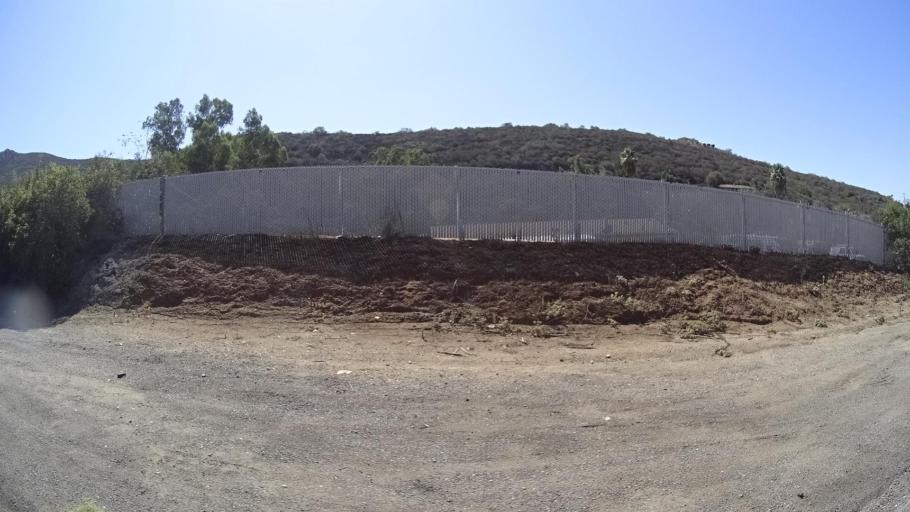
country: US
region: California
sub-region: San Diego County
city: Crest
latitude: 32.8089
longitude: -116.8863
